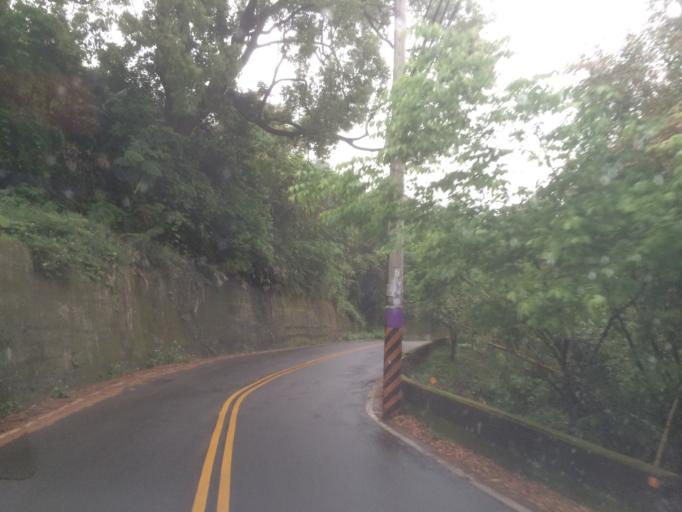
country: TW
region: Taiwan
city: Fengyuan
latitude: 24.1715
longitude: 120.8218
